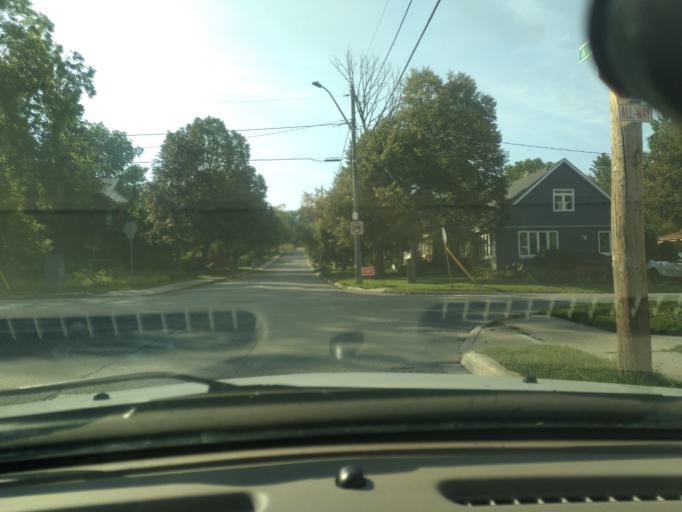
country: CA
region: Ontario
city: Barrie
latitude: 44.3701
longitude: -79.6890
